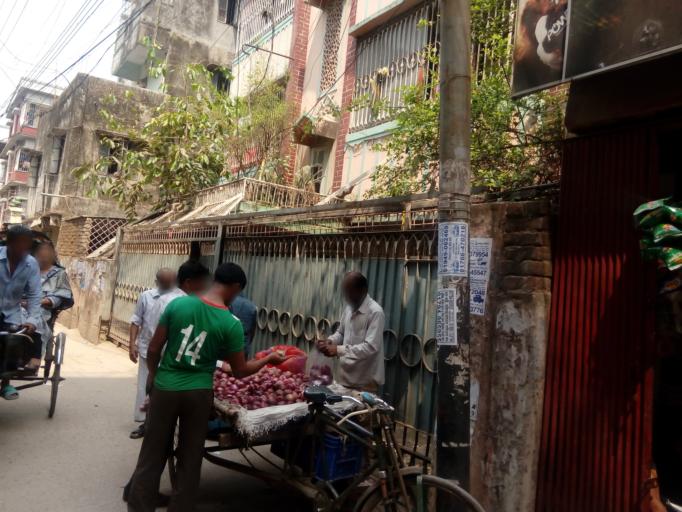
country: BD
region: Dhaka
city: Paltan
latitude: 23.7516
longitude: 90.4078
